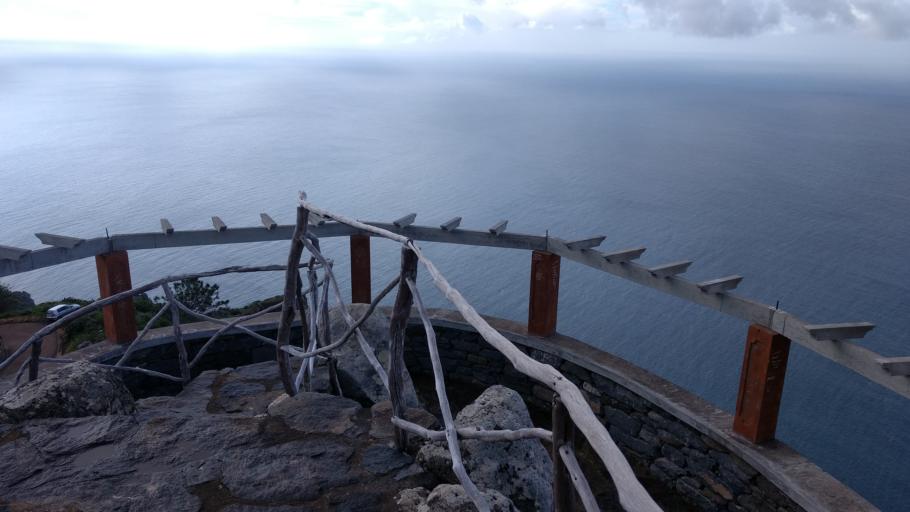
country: PT
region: Madeira
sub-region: Calheta
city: Faja da Ovelha
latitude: 32.7593
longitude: -17.2232
